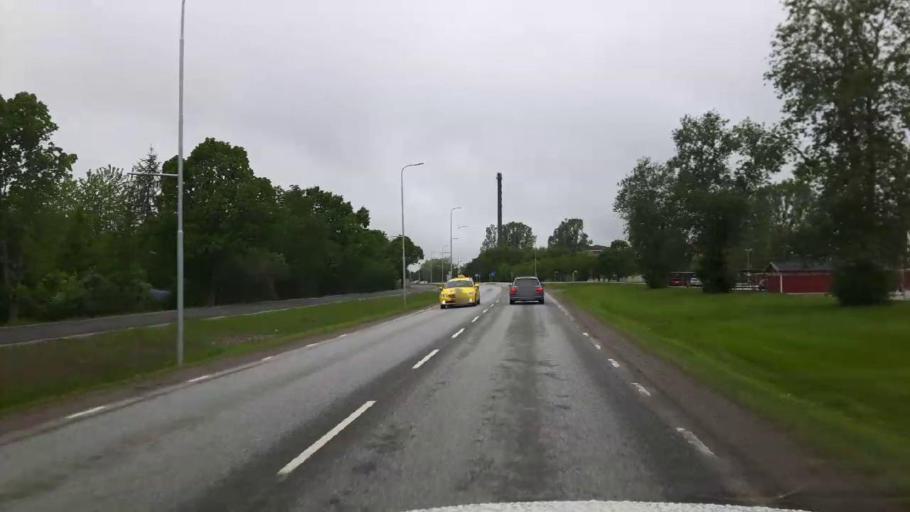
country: SE
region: Stockholm
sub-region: Upplands-Bro Kommun
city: Bro
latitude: 59.5130
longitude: 17.6471
